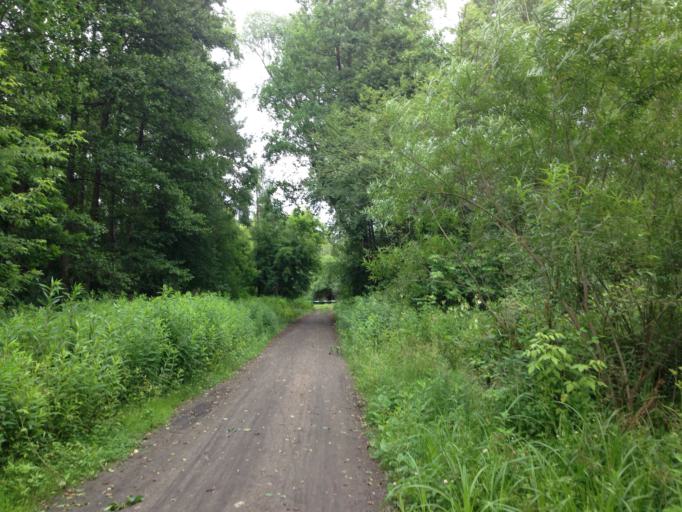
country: PL
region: Masovian Voivodeship
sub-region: Powiat warszawski zachodni
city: Babice
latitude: 52.2605
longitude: 20.8743
